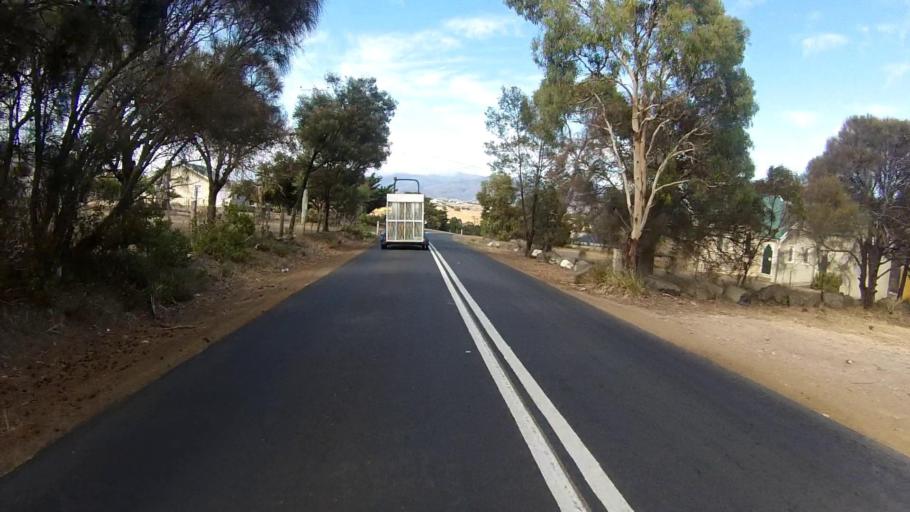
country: AU
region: Tasmania
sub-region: Brighton
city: Old Beach
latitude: -42.7495
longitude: 147.2801
